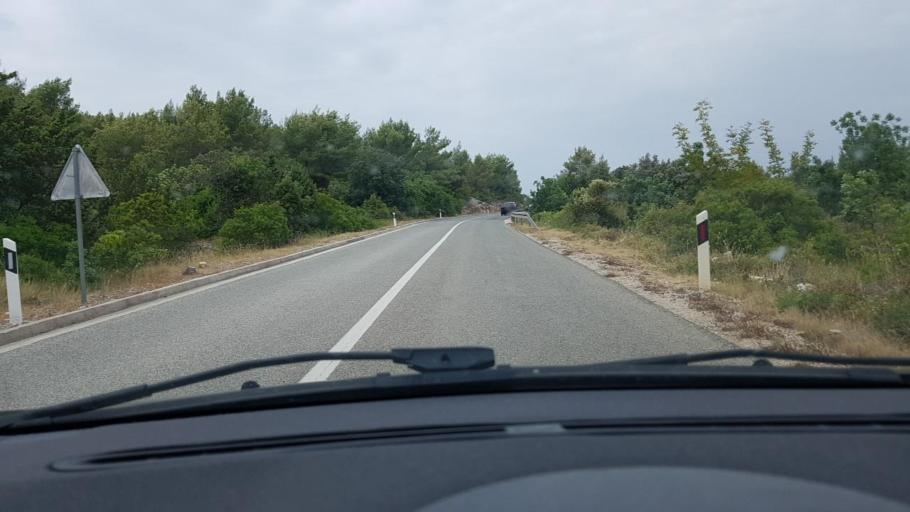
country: HR
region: Dubrovacko-Neretvanska
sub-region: Grad Korcula
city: Zrnovo
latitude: 42.9373
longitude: 17.0800
